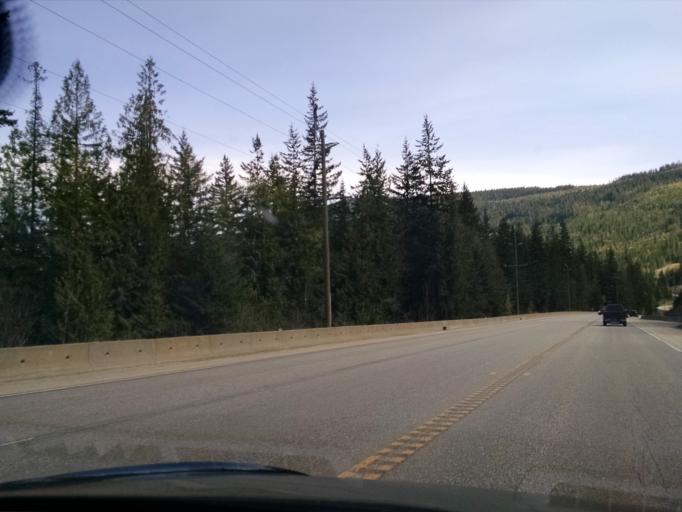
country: CA
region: British Columbia
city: Sicamous
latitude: 50.7894
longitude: -119.0960
